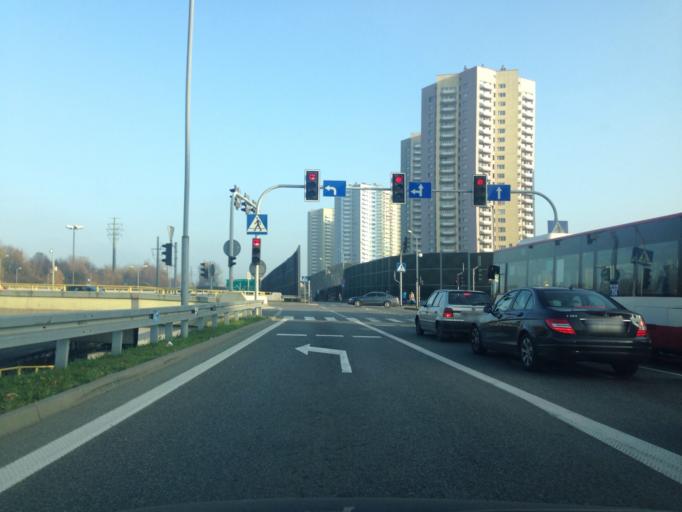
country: PL
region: Silesian Voivodeship
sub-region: Katowice
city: Katowice
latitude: 50.2621
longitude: 19.0347
